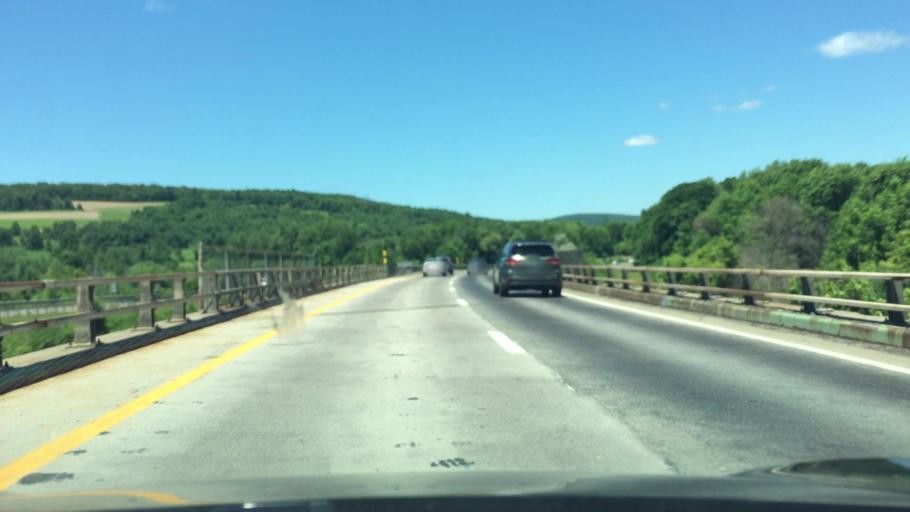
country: US
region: New York
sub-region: Cortland County
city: Homer
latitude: 42.6591
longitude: -76.1736
